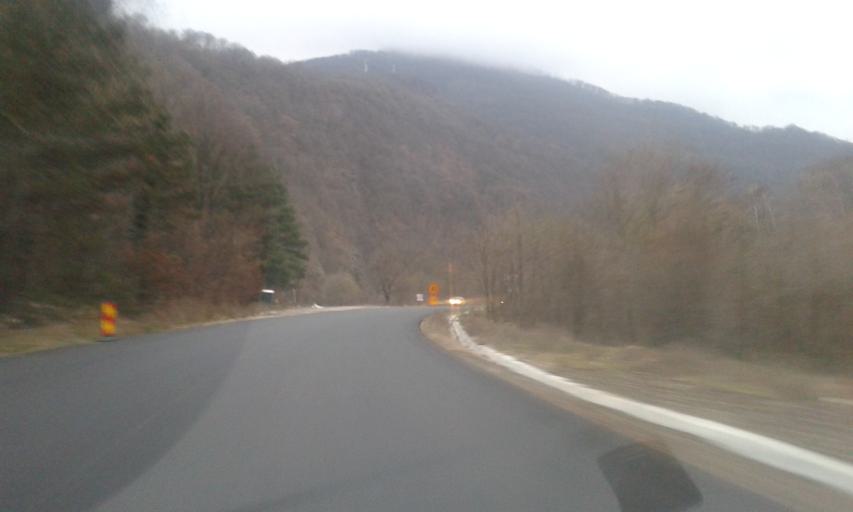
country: RO
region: Gorj
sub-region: Comuna Bumbesti-Jiu
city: Bumbesti-Jiu
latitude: 45.2710
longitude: 23.3807
